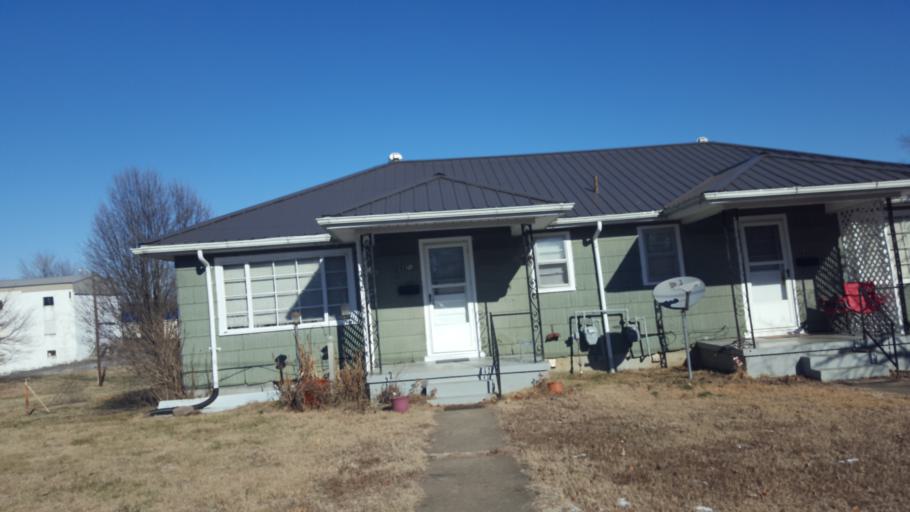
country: US
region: Kentucky
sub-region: Crittenden County
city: Marion
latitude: 37.3365
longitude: -88.0784
